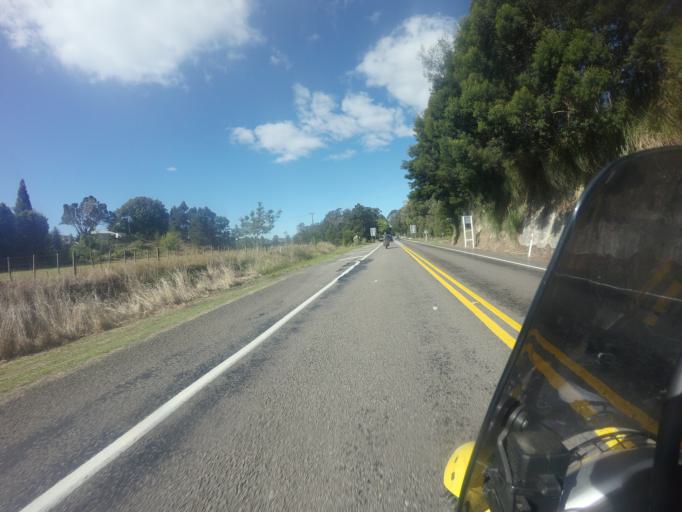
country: NZ
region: Bay of Plenty
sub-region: Opotiki District
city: Opotiki
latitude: -38.0445
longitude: 177.1480
